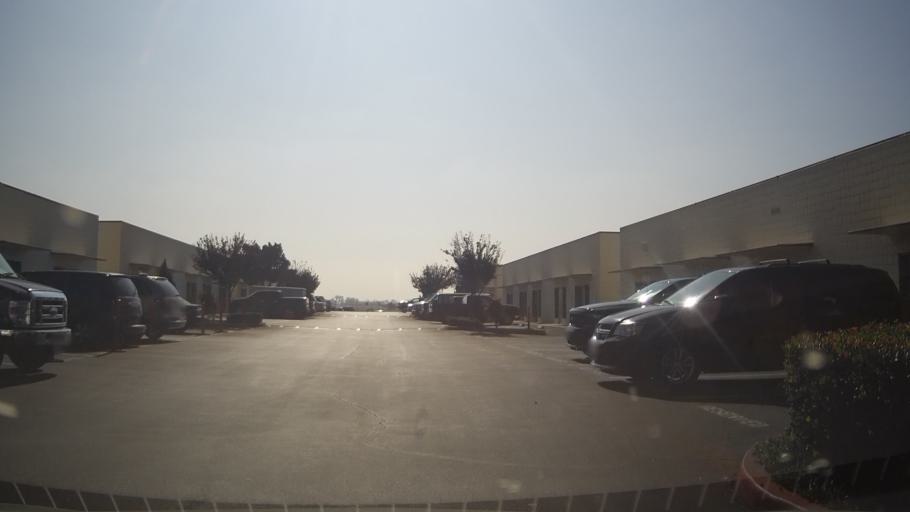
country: US
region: California
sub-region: San Diego County
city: San Diego
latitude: 32.8203
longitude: -117.1378
